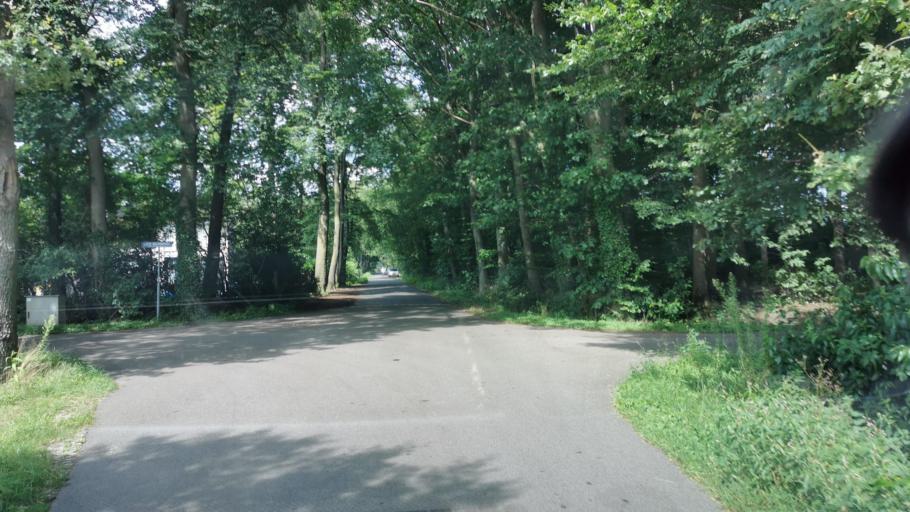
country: NL
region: Overijssel
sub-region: Gemeente Enschede
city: Enschede
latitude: 52.1666
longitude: 6.8683
